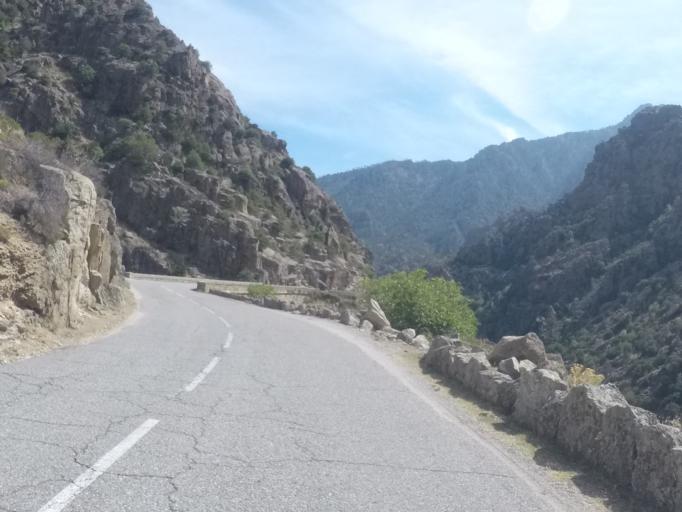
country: FR
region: Corsica
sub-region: Departement de la Haute-Corse
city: Corte
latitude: 42.3753
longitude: 9.0953
